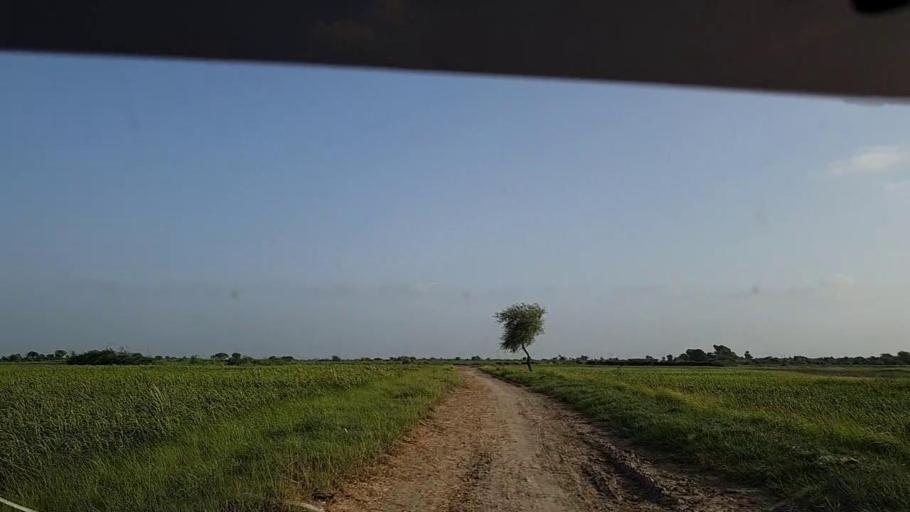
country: PK
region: Sindh
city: Badin
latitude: 24.5583
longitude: 68.8626
